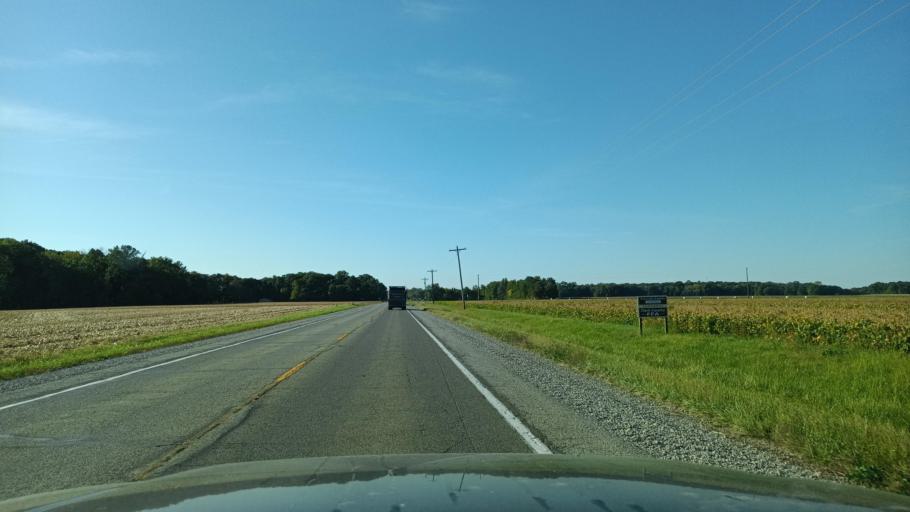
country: US
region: Illinois
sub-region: Clark County
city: Marshall
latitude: 39.4537
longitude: -87.6821
